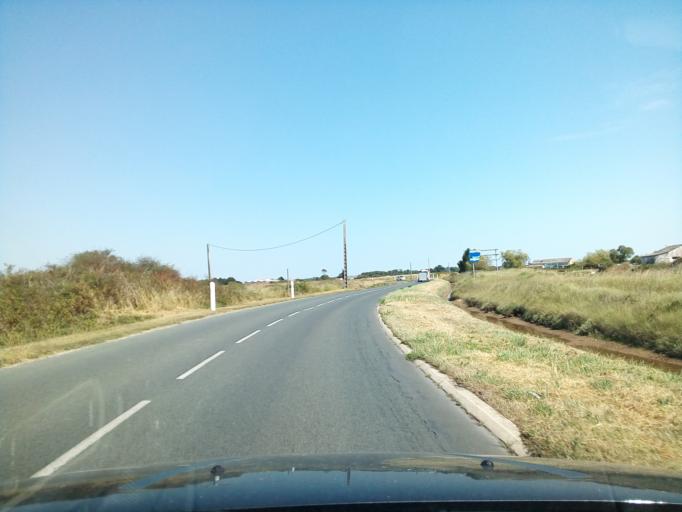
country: FR
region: Poitou-Charentes
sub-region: Departement de la Charente-Maritime
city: Boyard-Ville
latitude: 45.9688
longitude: -1.2770
